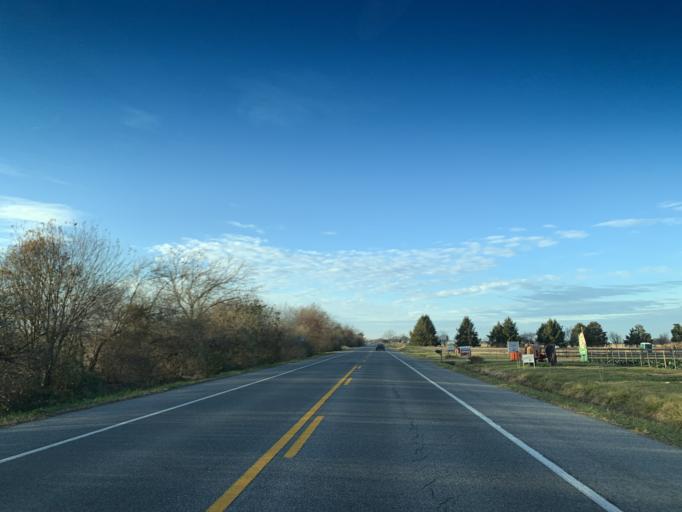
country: US
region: Maryland
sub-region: Kent County
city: Chestertown
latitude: 39.2535
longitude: -76.0785
